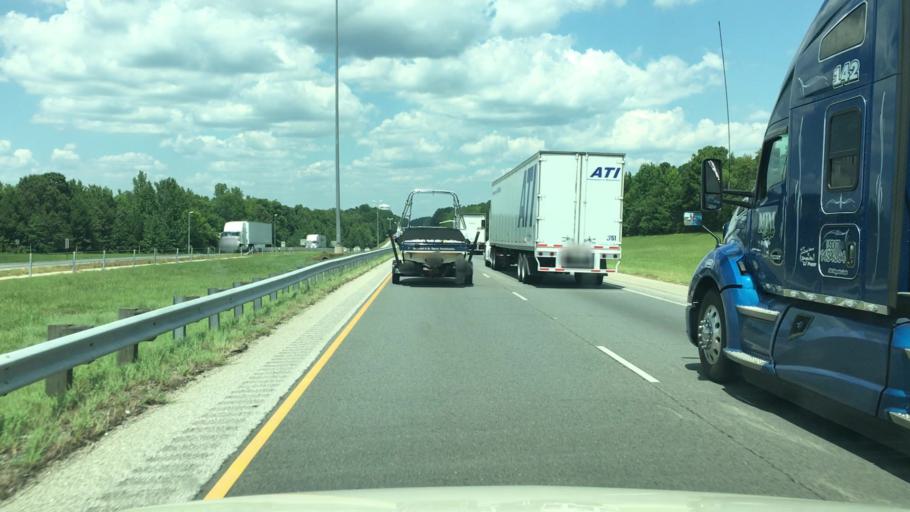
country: US
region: Arkansas
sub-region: Clark County
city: Arkadelphia
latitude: 34.1197
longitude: -93.0922
